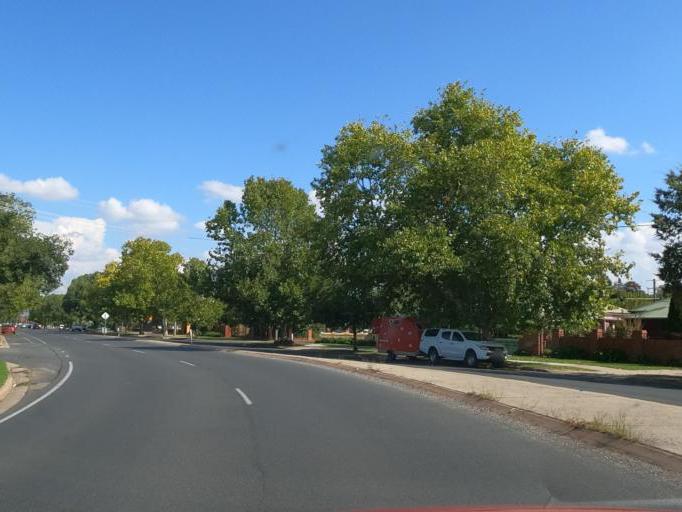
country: AU
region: New South Wales
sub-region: Albury Municipality
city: North Albury
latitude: -36.0640
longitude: 146.9247
